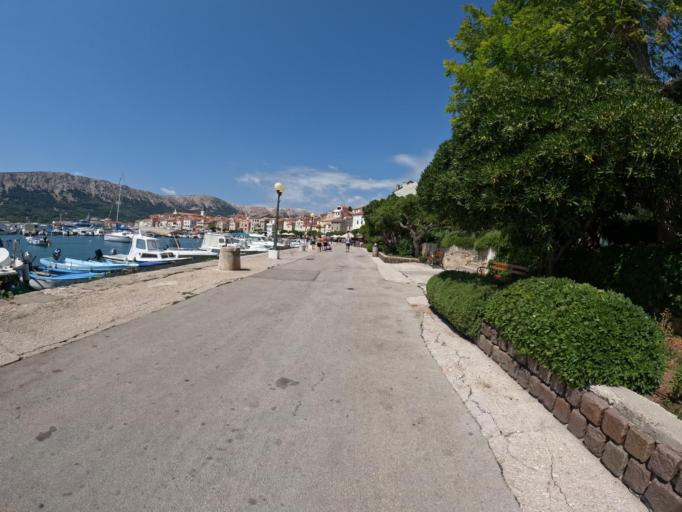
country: HR
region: Primorsko-Goranska
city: Punat
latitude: 44.9699
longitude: 14.7617
